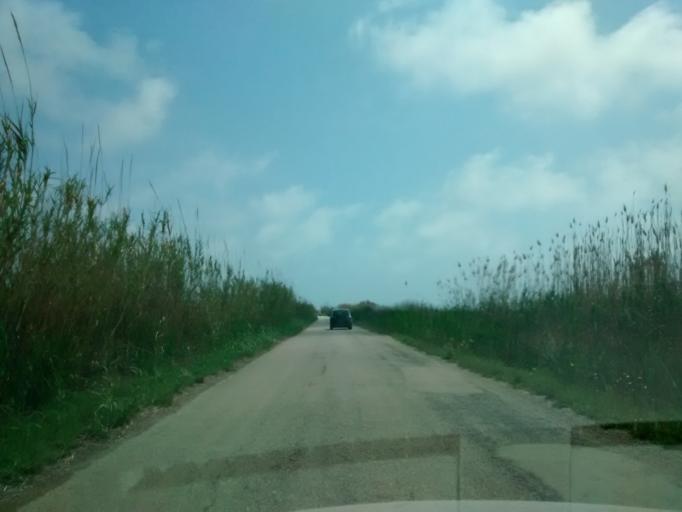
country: ES
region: Catalonia
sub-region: Provincia de Tarragona
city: Deltebre
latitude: 40.6920
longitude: 0.8423
